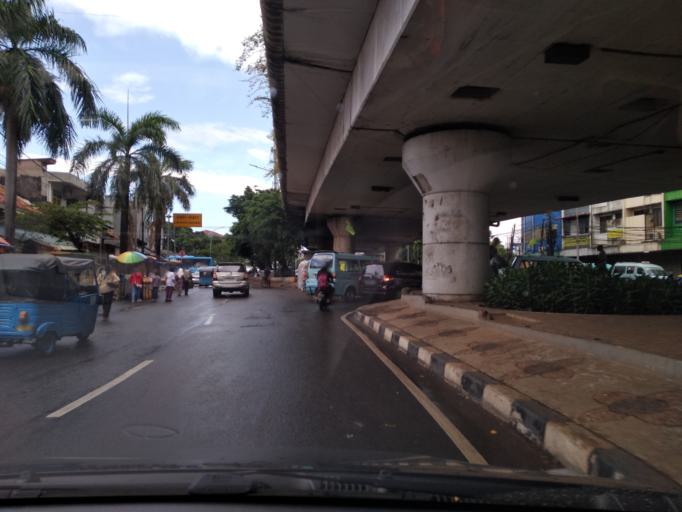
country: ID
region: Jakarta Raya
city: Jakarta
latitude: -6.2247
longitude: 106.8657
